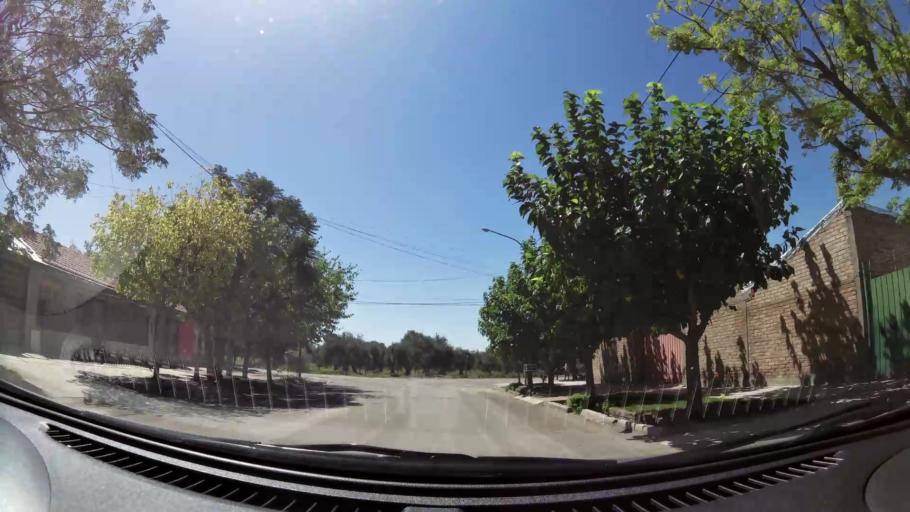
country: AR
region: Mendoza
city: Villa Nueva
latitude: -32.8782
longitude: -68.7931
